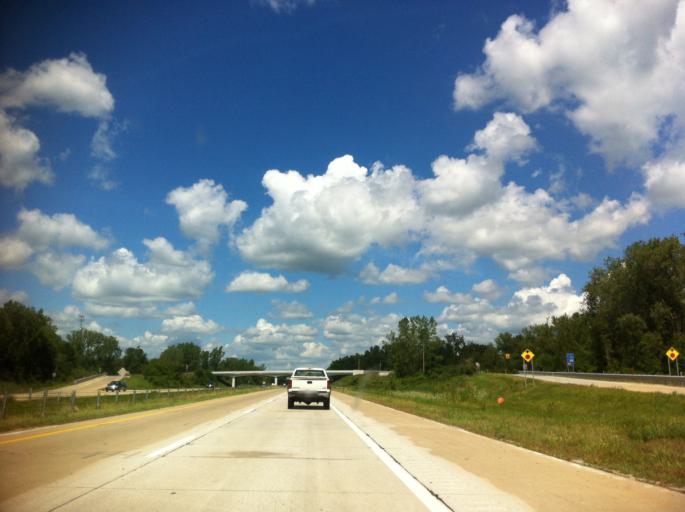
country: US
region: Michigan
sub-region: Monroe County
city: Petersburg
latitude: 41.8400
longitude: -83.6714
